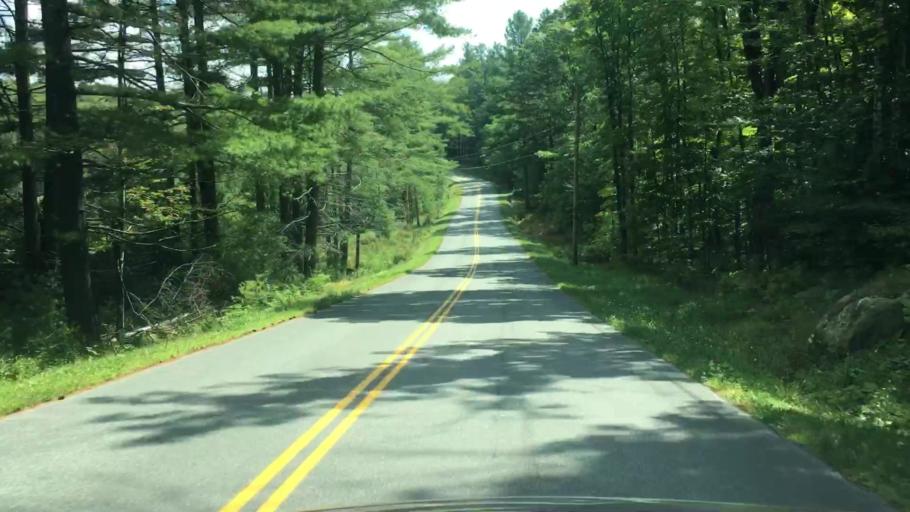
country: US
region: Vermont
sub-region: Windham County
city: Dover
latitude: 42.8184
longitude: -72.7589
